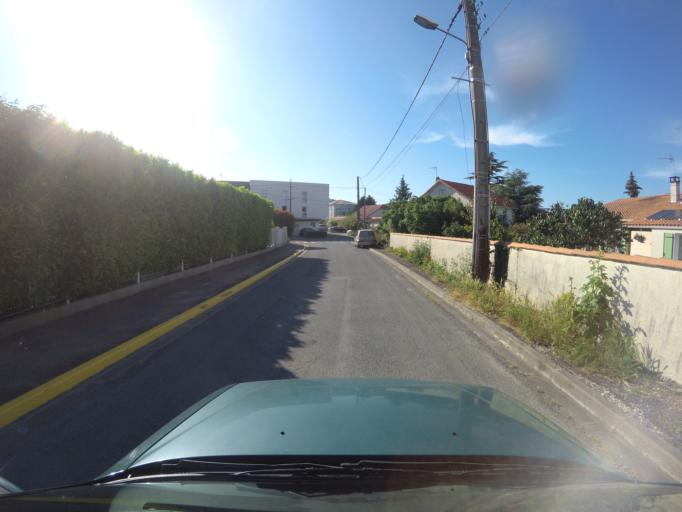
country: FR
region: Poitou-Charentes
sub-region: Departement de la Charente-Maritime
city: Royan
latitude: 45.6365
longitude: -1.0254
